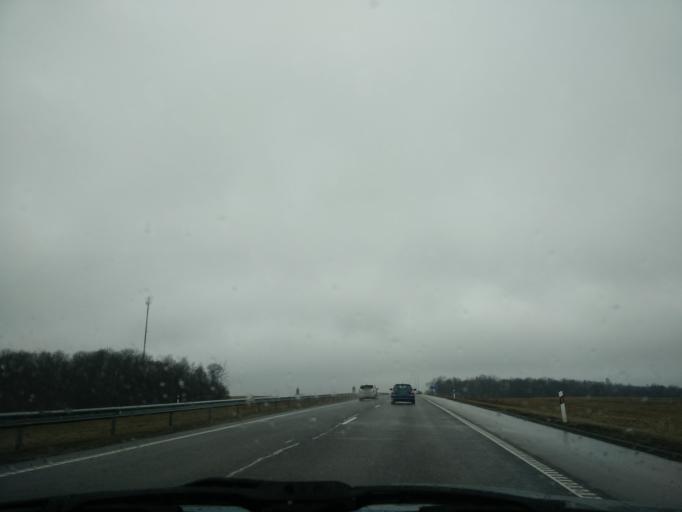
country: LT
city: Skaudvile
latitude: 55.5032
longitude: 22.4580
